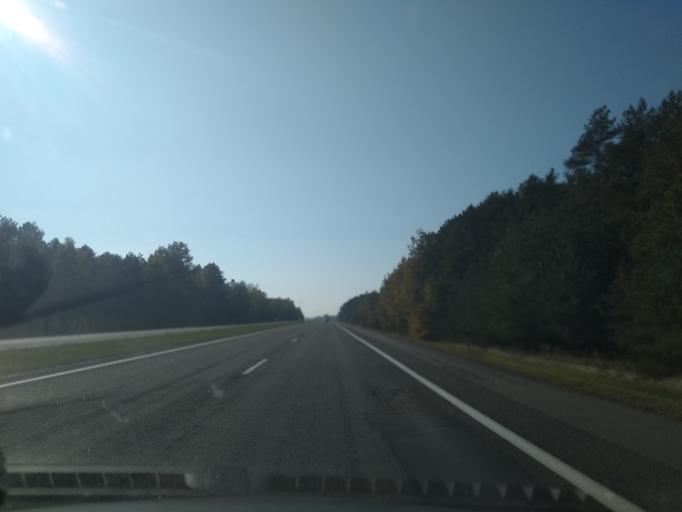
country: BY
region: Brest
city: Antopal'
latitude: 52.3409
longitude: 24.6516
